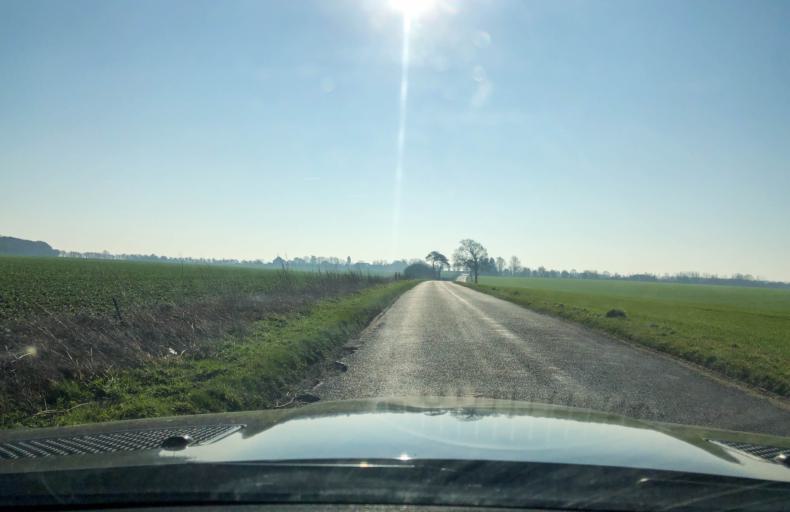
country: GB
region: England
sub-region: Warwickshire
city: Wellesbourne Mountford
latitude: 52.1736
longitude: -1.5258
